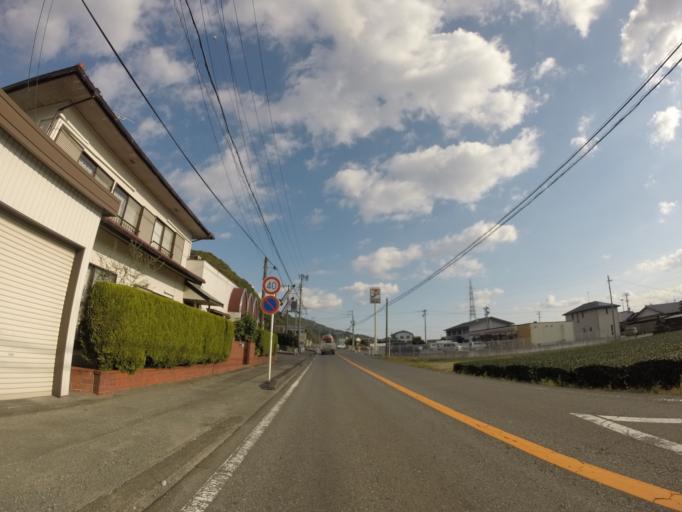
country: JP
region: Shizuoka
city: Kanaya
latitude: 34.8721
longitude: 138.1149
